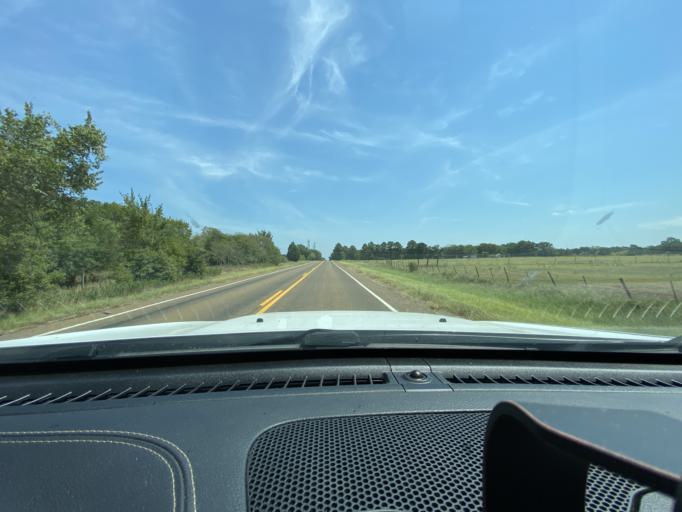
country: US
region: Texas
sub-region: Bastrop County
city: Smithville
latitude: 30.0667
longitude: -97.0963
